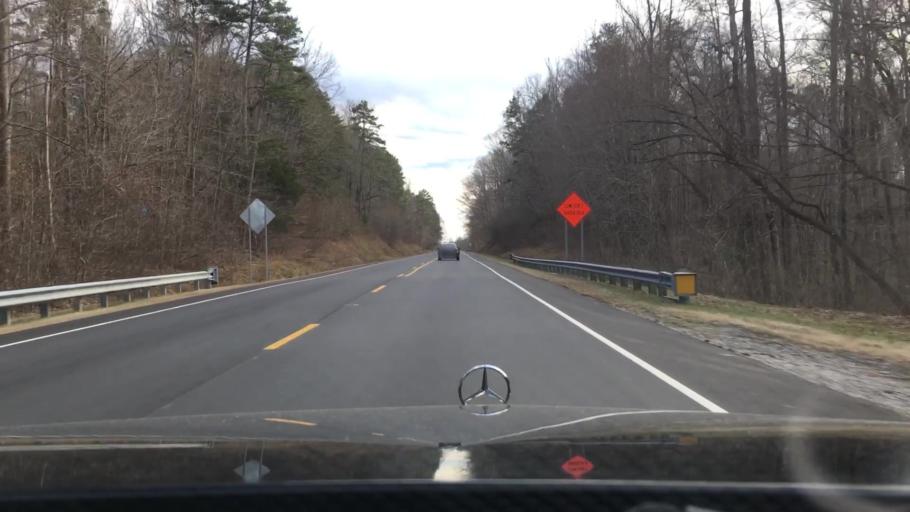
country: US
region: North Carolina
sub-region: Caswell County
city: Yanceyville
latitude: 36.4760
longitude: -79.3784
